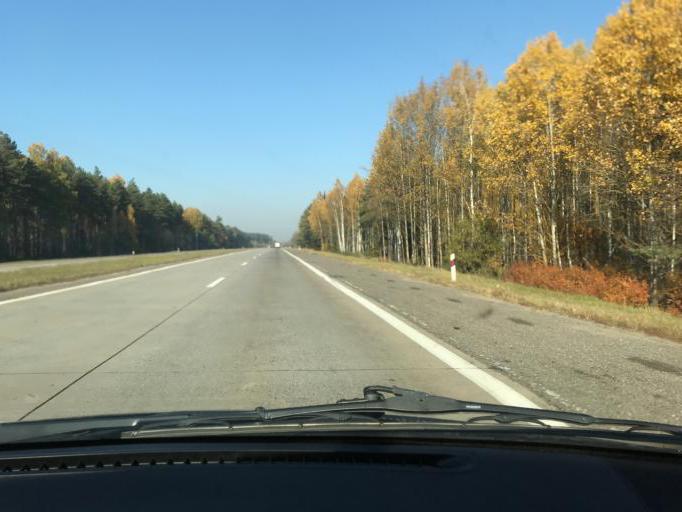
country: BY
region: Minsk
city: Uzda
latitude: 53.3855
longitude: 27.4881
